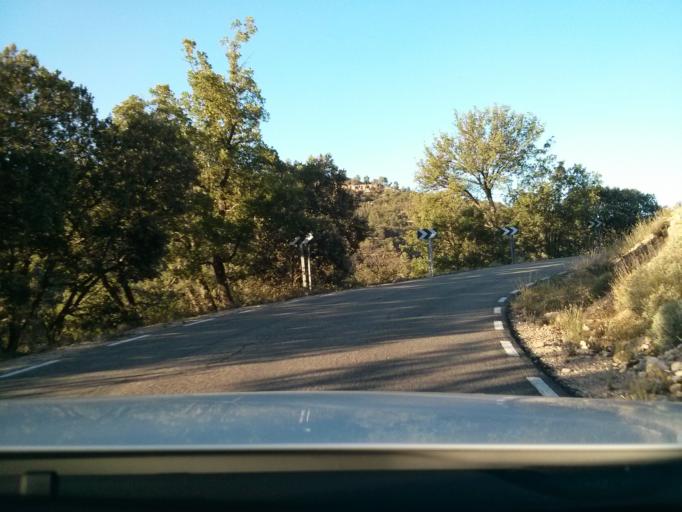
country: ES
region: Castille-La Mancha
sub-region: Provincia de Guadalajara
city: Mantiel
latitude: 40.6337
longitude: -2.6431
